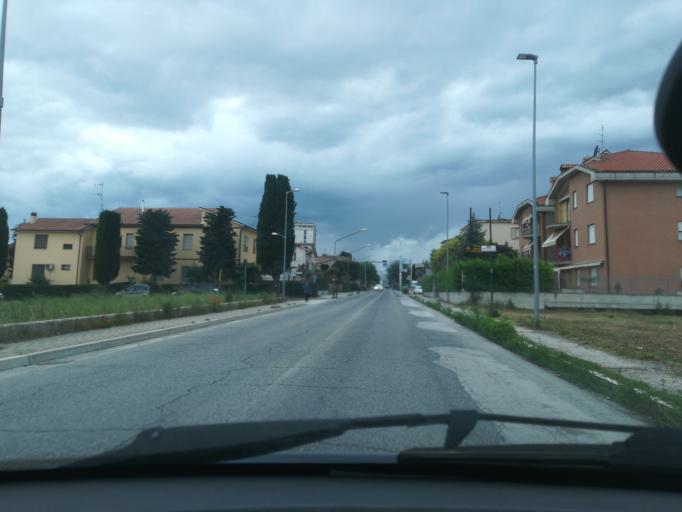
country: IT
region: The Marches
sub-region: Provincia di Macerata
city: Casette Verdini
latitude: 43.2539
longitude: 13.4099
